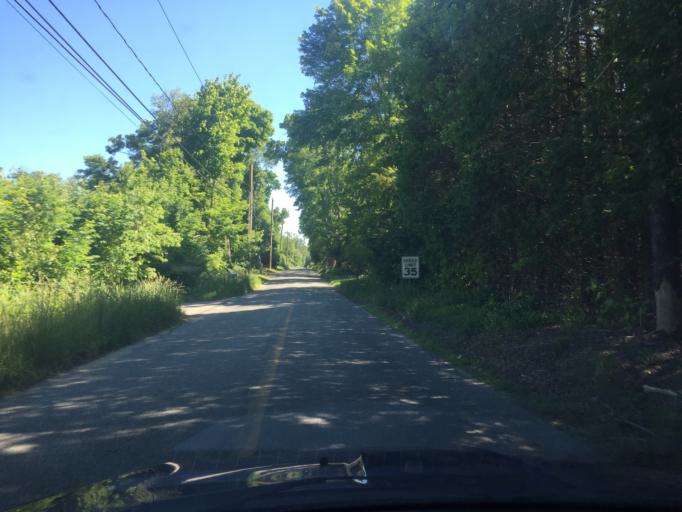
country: US
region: Rhode Island
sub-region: Washington County
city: Hopkinton
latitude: 41.4661
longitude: -71.8146
